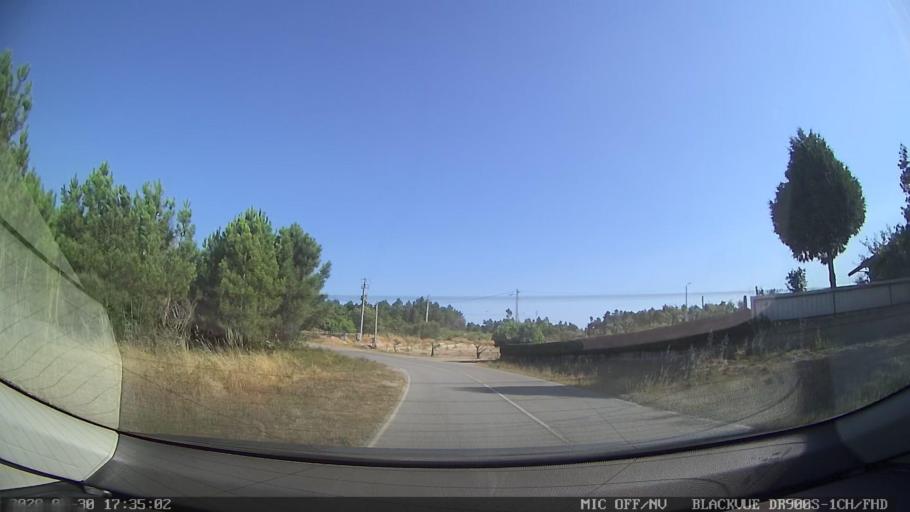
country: PT
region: Vila Real
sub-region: Murca
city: Murca
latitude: 41.3568
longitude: -7.4900
